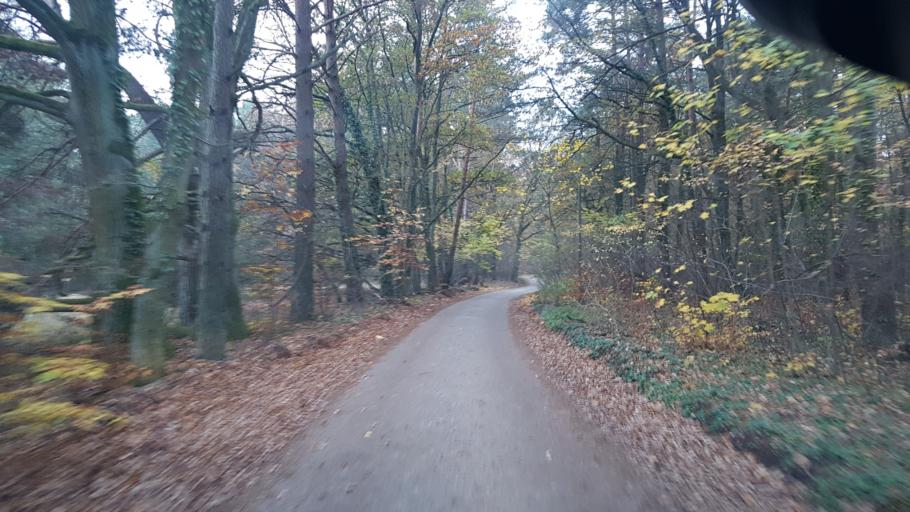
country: DE
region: Brandenburg
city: Lindow
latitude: 52.9920
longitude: 12.9684
